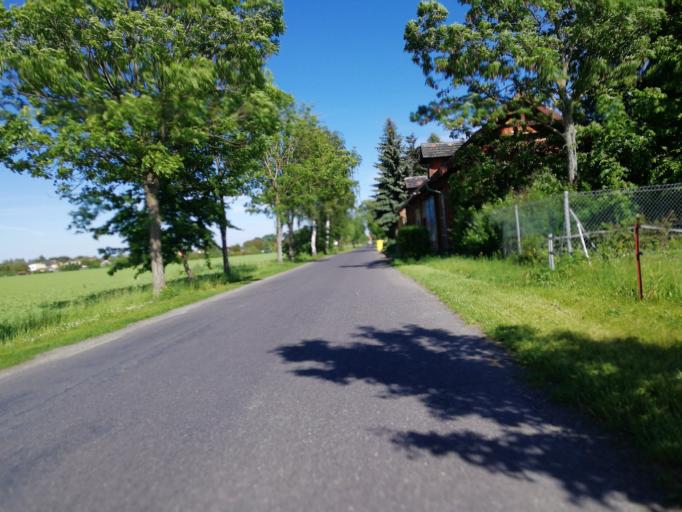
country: DE
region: Brandenburg
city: Calau
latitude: 51.7462
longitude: 13.9362
